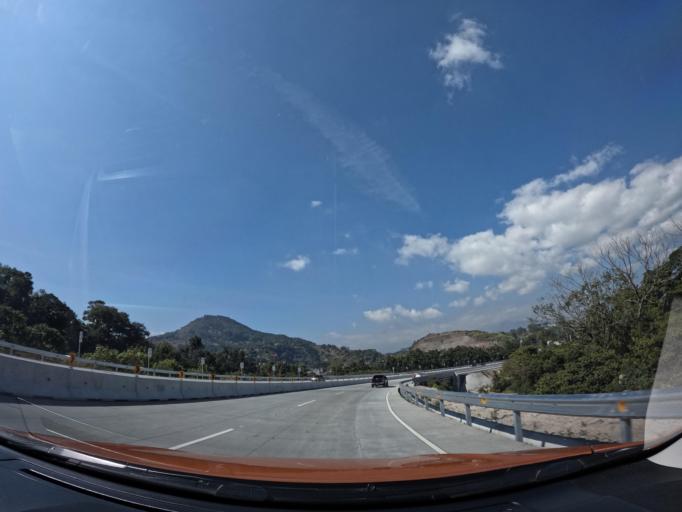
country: GT
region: Guatemala
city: Villa Canales
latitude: 14.4891
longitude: -90.5337
